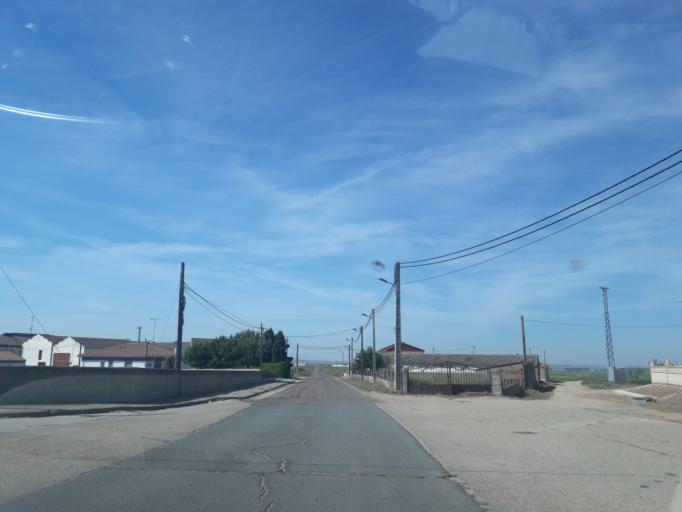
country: ES
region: Castille and Leon
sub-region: Provincia de Salamanca
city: Villoruela
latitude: 41.0054
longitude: -5.3972
